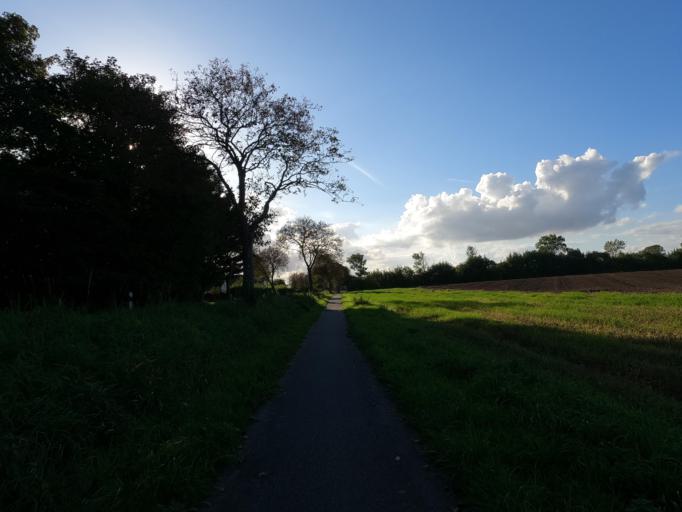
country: DE
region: Schleswig-Holstein
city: Neukirchen
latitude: 54.3249
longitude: 11.0268
